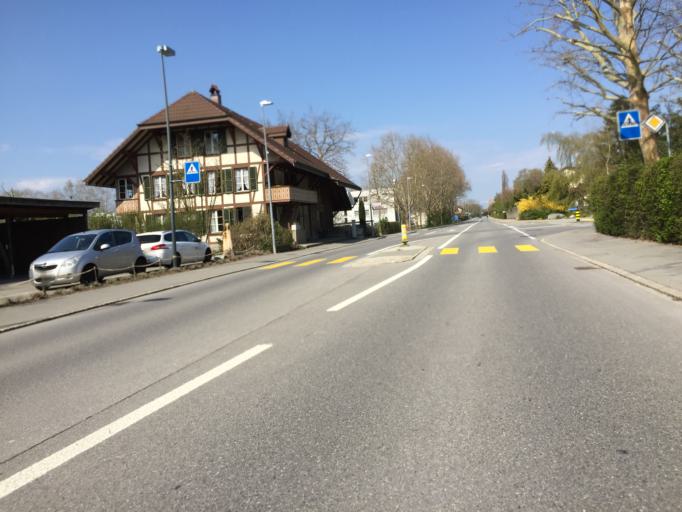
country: CH
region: Bern
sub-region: Bern-Mittelland District
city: Urtenen
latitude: 47.0206
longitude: 7.4954
